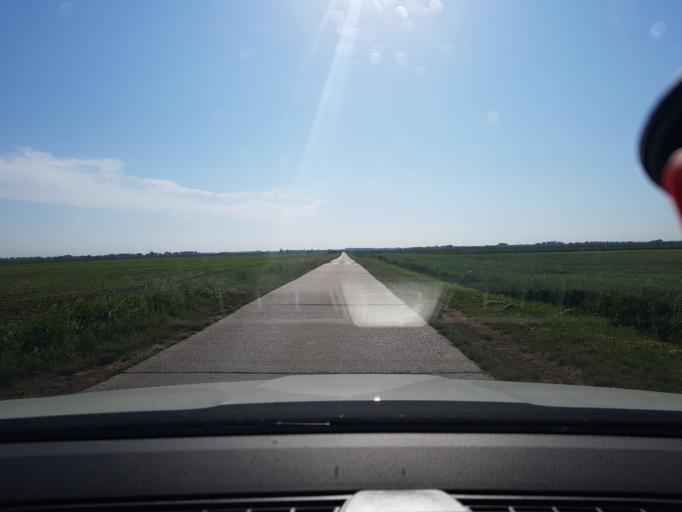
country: HU
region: Tolna
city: Szekszard
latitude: 46.2839
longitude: 18.6878
